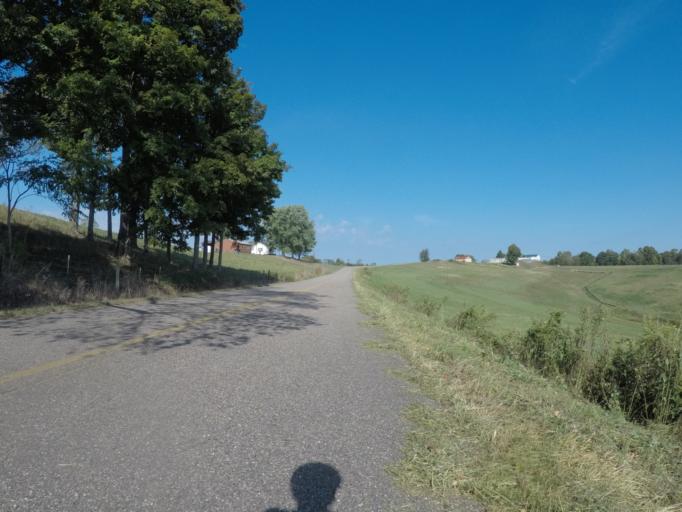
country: US
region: West Virginia
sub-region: Cabell County
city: Lesage
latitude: 38.6471
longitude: -82.4185
